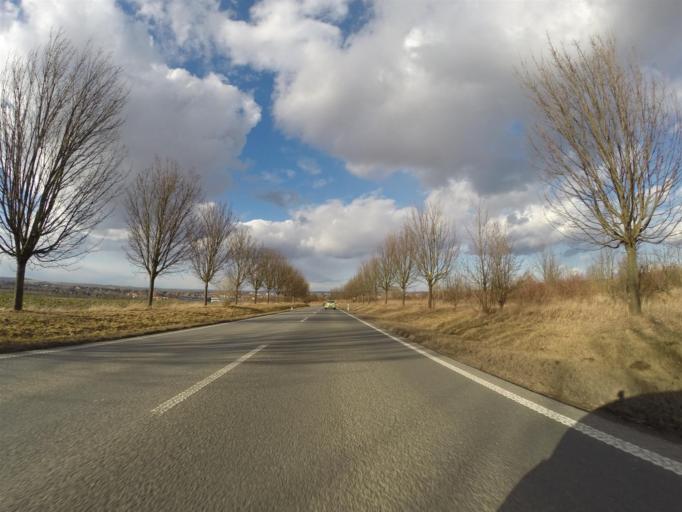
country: DE
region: Thuringia
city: Apolda
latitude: 51.0071
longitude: 11.5156
